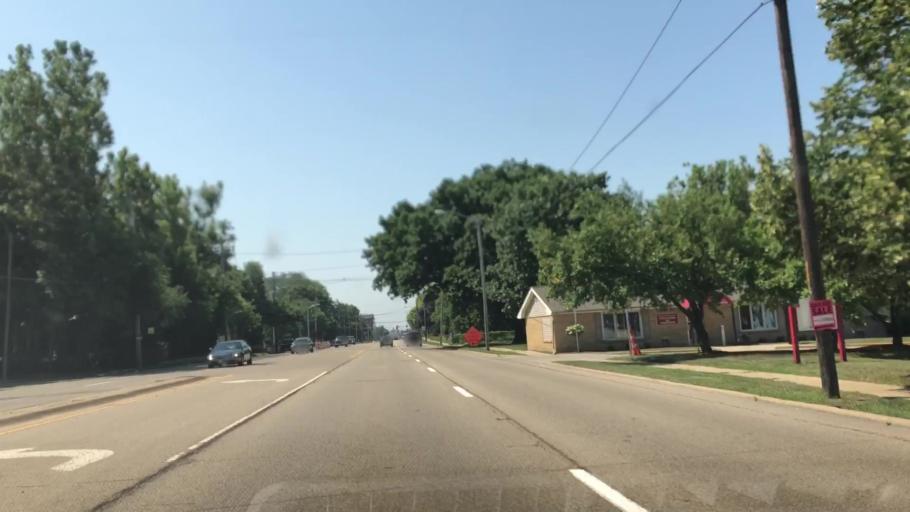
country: US
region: Illinois
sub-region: McLean County
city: Normal
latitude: 40.5198
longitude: -88.9952
